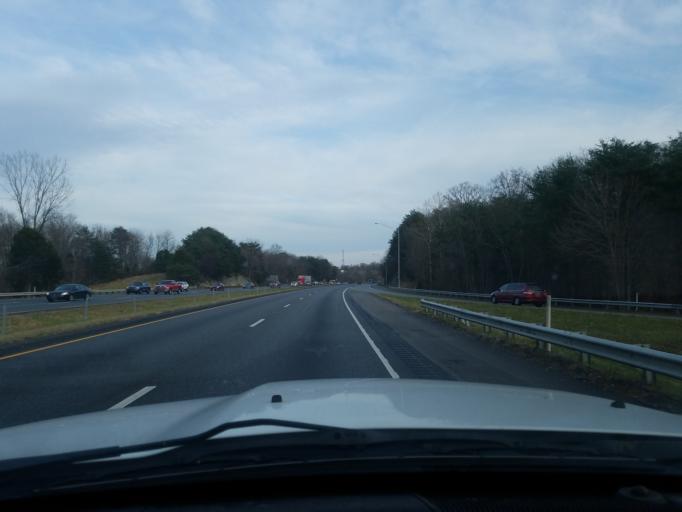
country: US
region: Indiana
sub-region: Floyd County
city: New Albany
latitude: 38.3040
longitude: -85.8851
